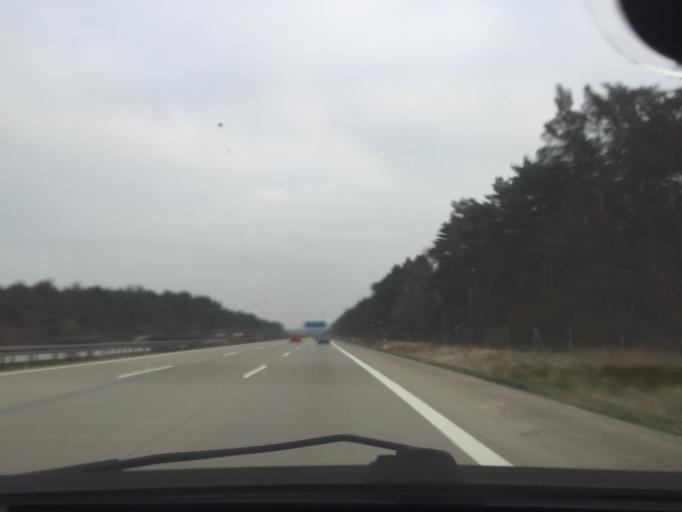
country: DE
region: Brandenburg
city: Wenzlow
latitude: 52.2829
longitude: 12.4480
